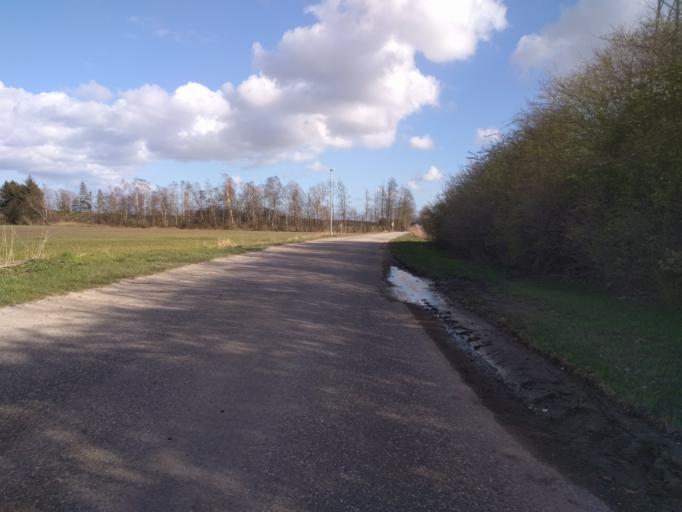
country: DK
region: South Denmark
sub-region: Odense Kommune
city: Neder Holluf
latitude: 55.3698
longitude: 10.5133
